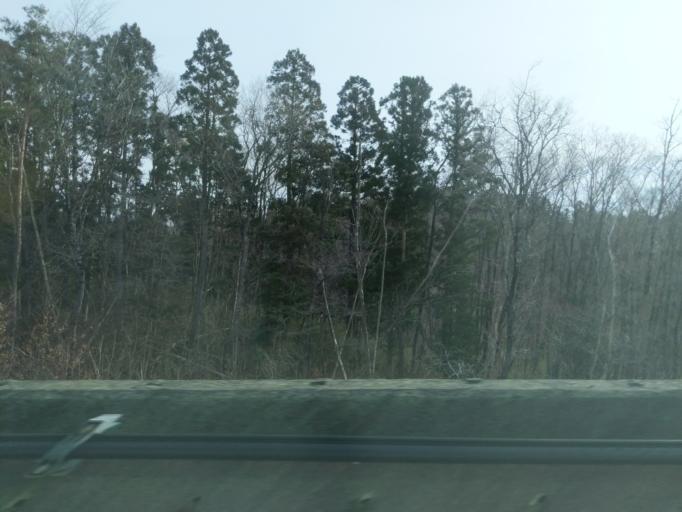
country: JP
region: Miyagi
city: Kogota
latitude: 38.7307
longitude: 141.0614
